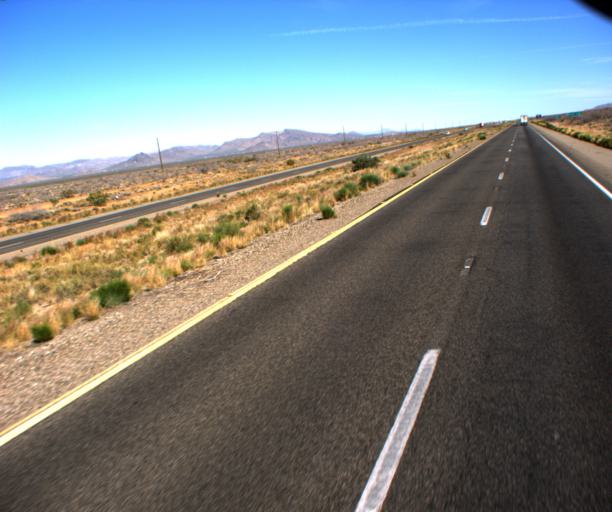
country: US
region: Arizona
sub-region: Mohave County
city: Golden Valley
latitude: 35.2766
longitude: -114.1720
